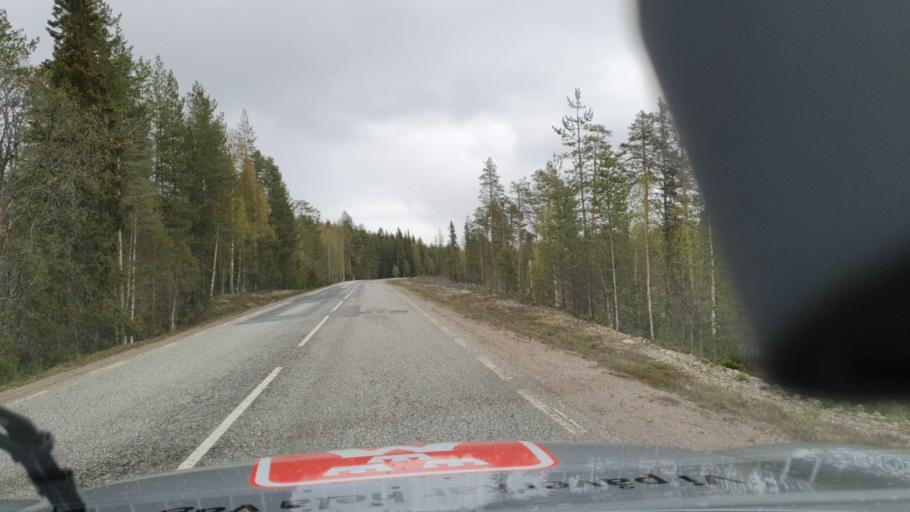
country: SE
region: Vaesternorrland
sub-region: Solleftea Kommun
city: Solleftea
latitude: 63.6550
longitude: 17.3030
